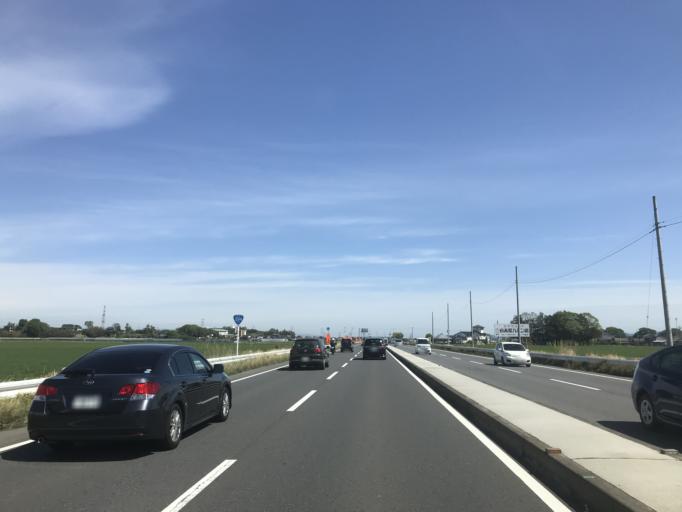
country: JP
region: Ibaraki
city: Shimodate
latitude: 36.2114
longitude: 139.9853
